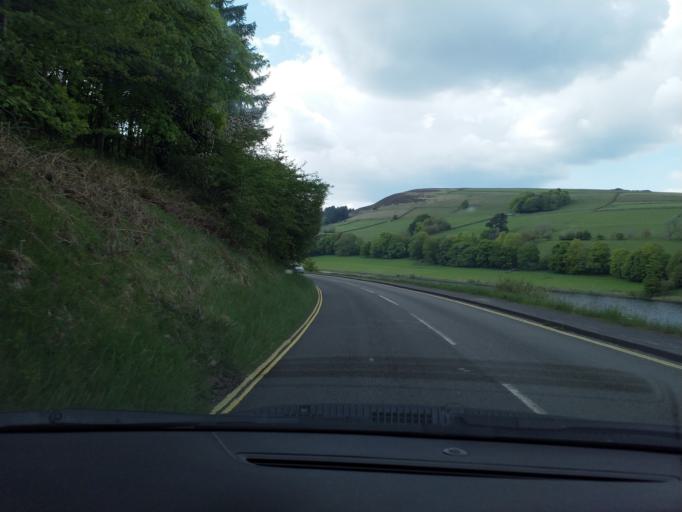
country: GB
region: England
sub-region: Derbyshire
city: Hope Valley
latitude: 53.3914
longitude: -1.7266
